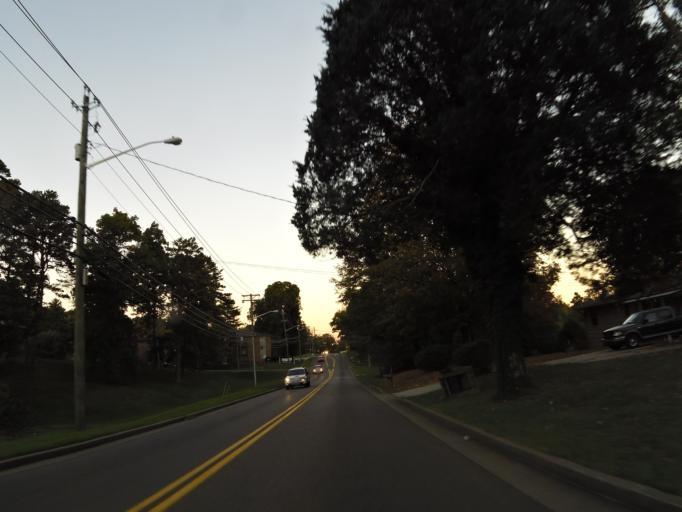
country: US
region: Tennessee
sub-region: Knox County
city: Knoxville
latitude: 36.0233
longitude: -83.9573
